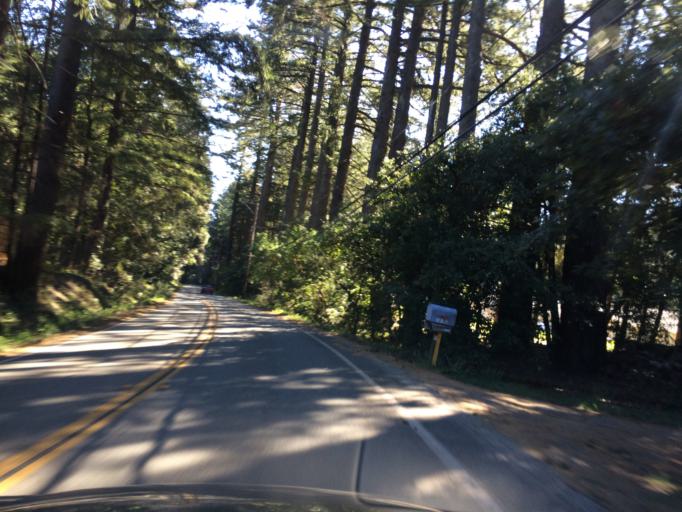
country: US
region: California
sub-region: Santa Cruz County
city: Brookdale
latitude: 37.0927
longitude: -122.1410
